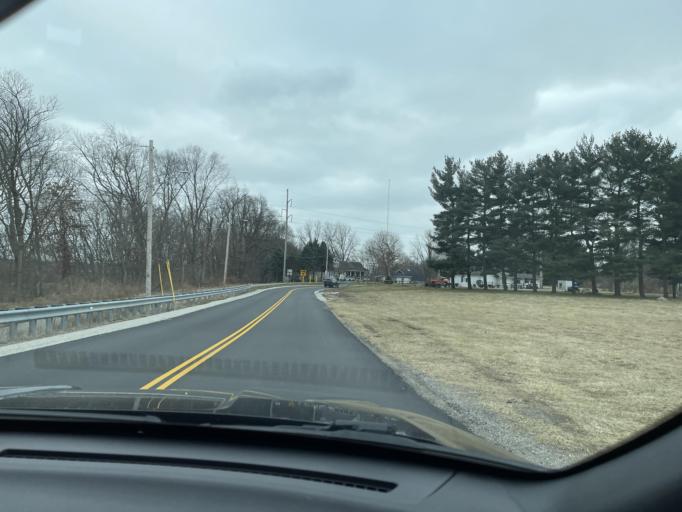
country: US
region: Illinois
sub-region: Sangamon County
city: Rochester
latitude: 39.7735
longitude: -89.5800
